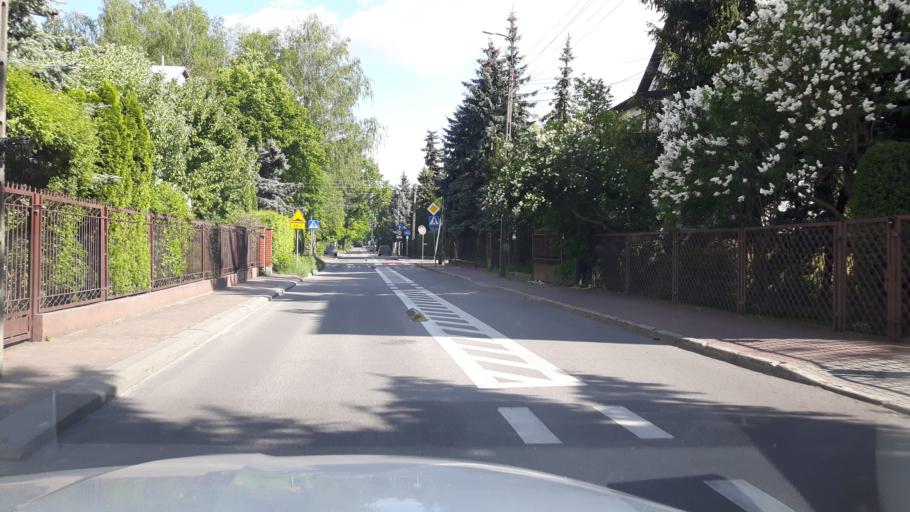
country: PL
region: Masovian Voivodeship
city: Zielonka
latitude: 52.3058
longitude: 21.1546
